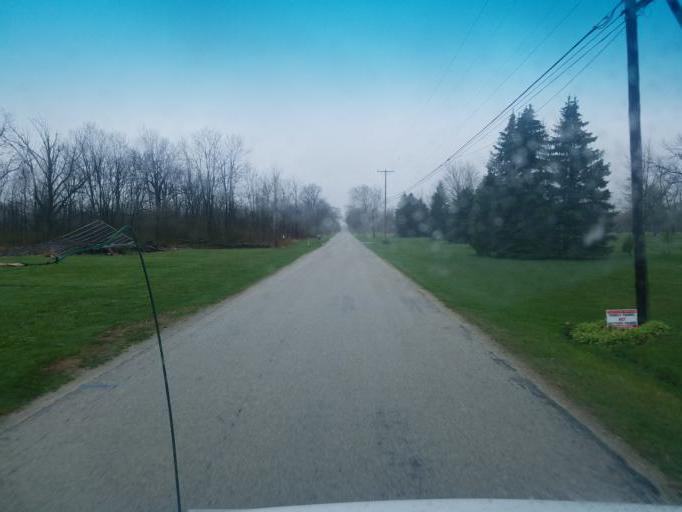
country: US
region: Ohio
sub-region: Wood County
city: North Baltimore
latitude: 41.2461
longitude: -83.6308
